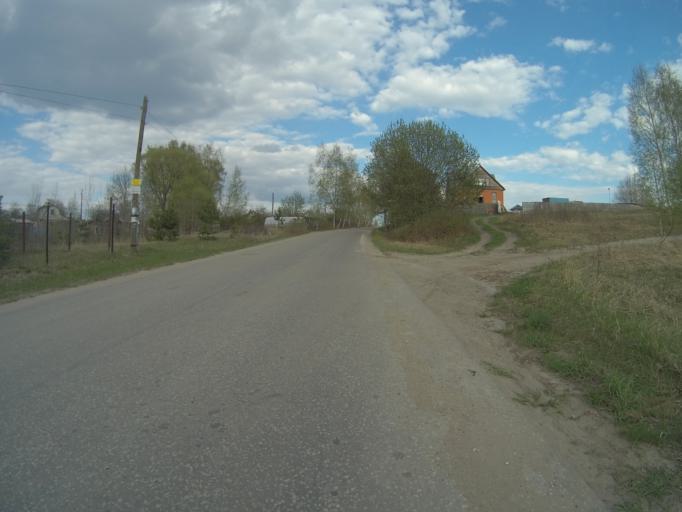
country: RU
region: Vladimir
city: Kommunar
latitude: 56.0350
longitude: 40.4483
